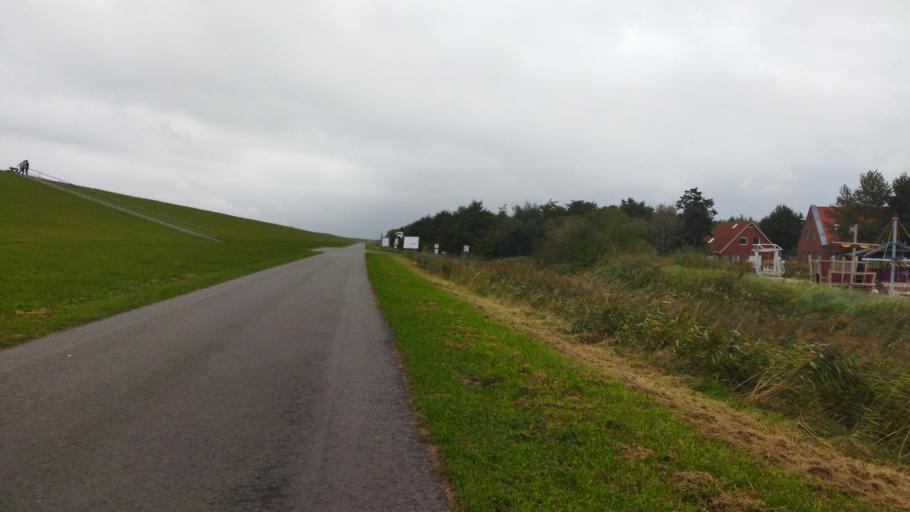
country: NL
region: Groningen
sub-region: Gemeente Delfzijl
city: Delfzijl
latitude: 53.4201
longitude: 7.0138
